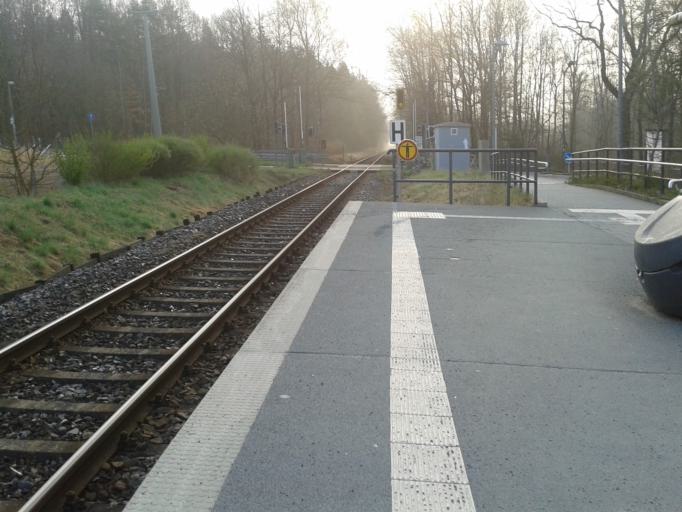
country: DE
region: Bavaria
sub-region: Regierungsbezirk Mittelfranken
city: Seukendorf
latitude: 49.4646
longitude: 10.8872
